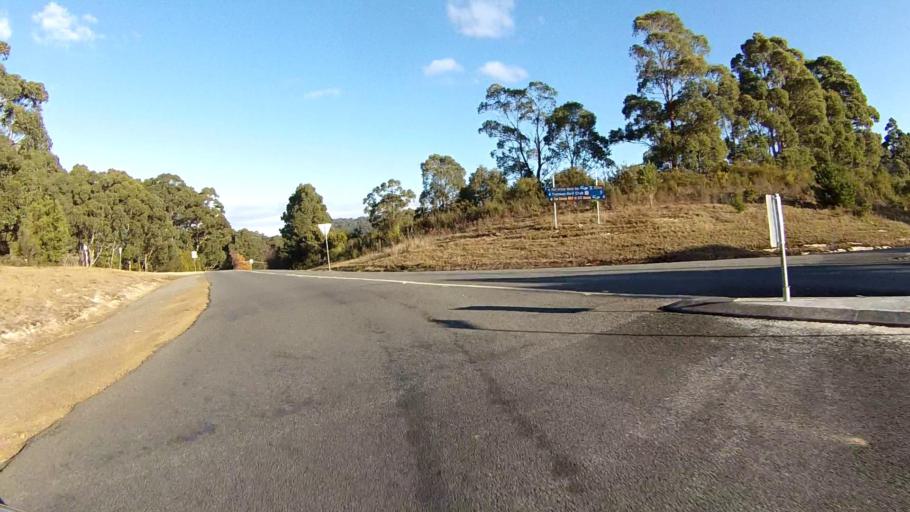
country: AU
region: Tasmania
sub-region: Clarence
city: Sandford
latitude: -43.1430
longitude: 147.8452
